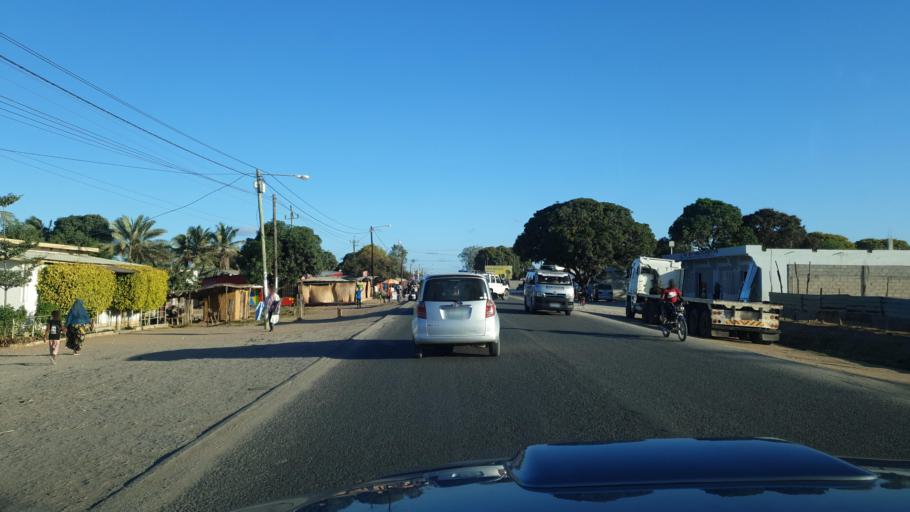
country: MZ
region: Nampula
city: Nacala
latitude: -14.5774
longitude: 40.6816
